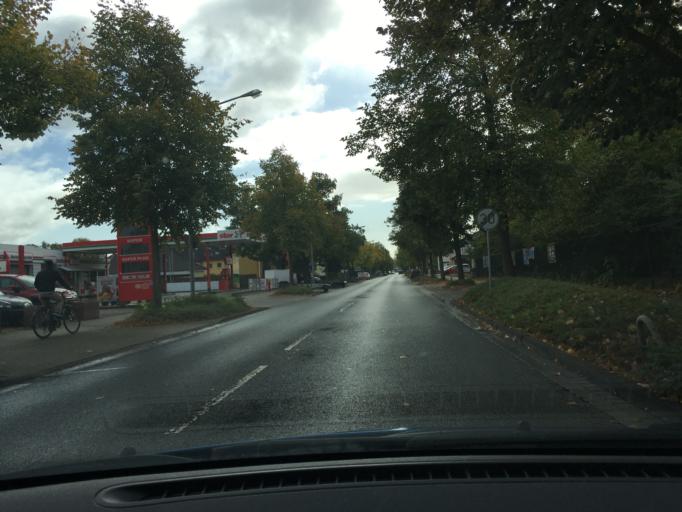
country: DE
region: Lower Saxony
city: Uelzen
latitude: 52.9719
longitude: 10.5708
